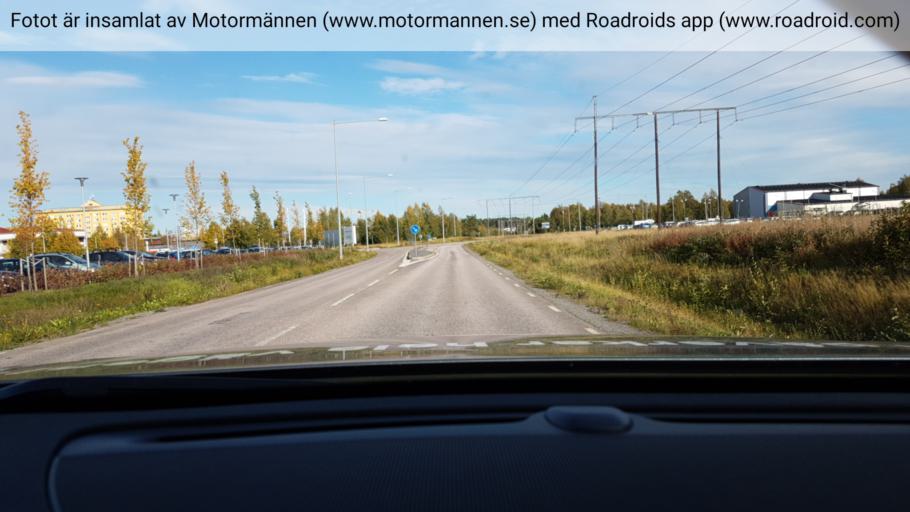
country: SE
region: Norrbotten
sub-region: Lulea Kommun
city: Bergnaset
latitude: 65.6154
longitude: 22.1254
